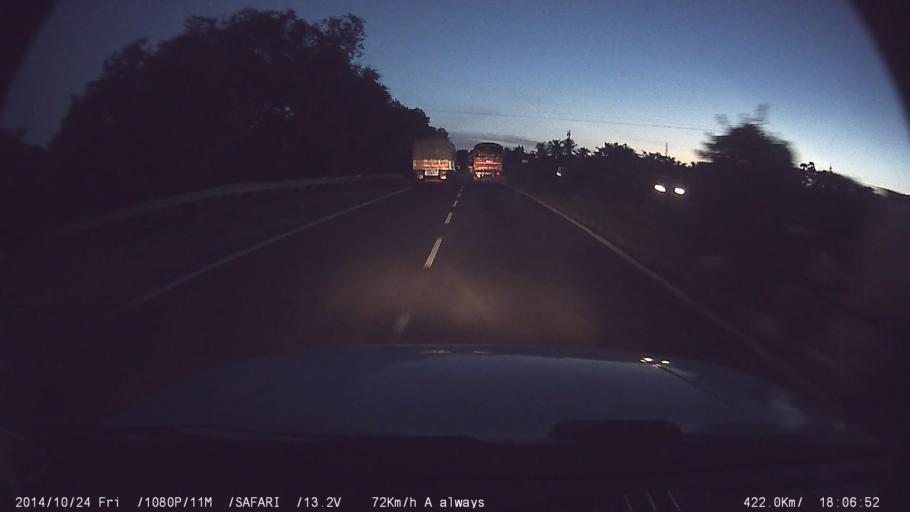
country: IN
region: Tamil Nadu
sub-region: Kancheepuram
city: Madurantakam
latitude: 12.5800
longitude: 79.9184
